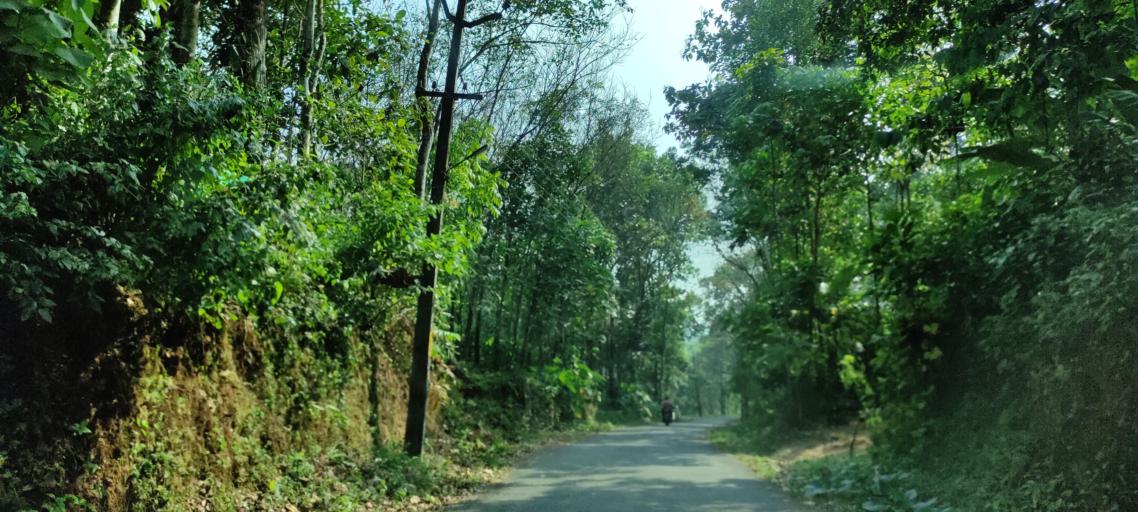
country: IN
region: Kerala
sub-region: Ernakulam
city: Piravam
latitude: 9.8067
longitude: 76.5259
